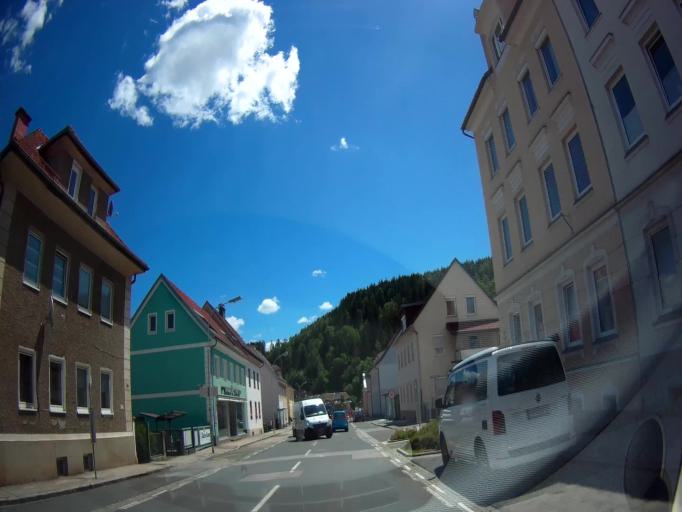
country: AT
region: Carinthia
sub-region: Politischer Bezirk Sankt Veit an der Glan
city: Sankt Veit an der Glan
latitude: 46.7624
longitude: 14.3645
